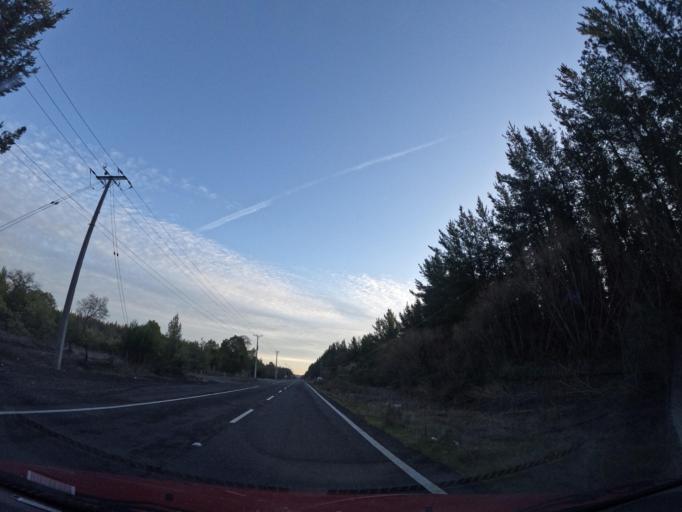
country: CL
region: Biobio
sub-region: Provincia de Biobio
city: Los Angeles
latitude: -37.3724
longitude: -71.8821
